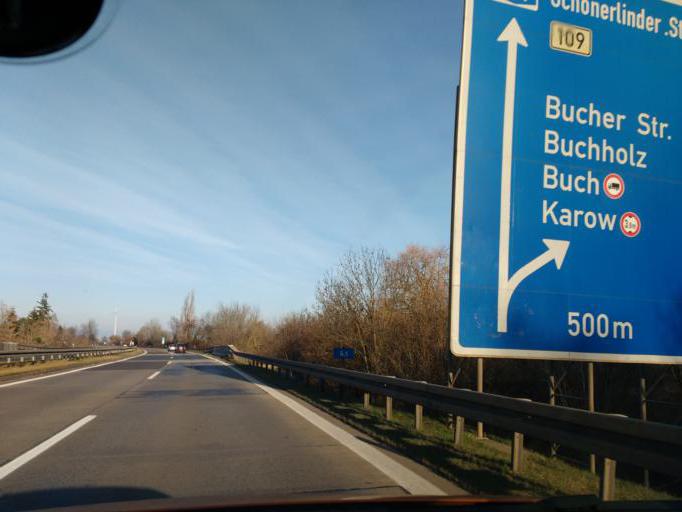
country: DE
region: Berlin
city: Blankenburg
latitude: 52.6074
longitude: 13.4494
